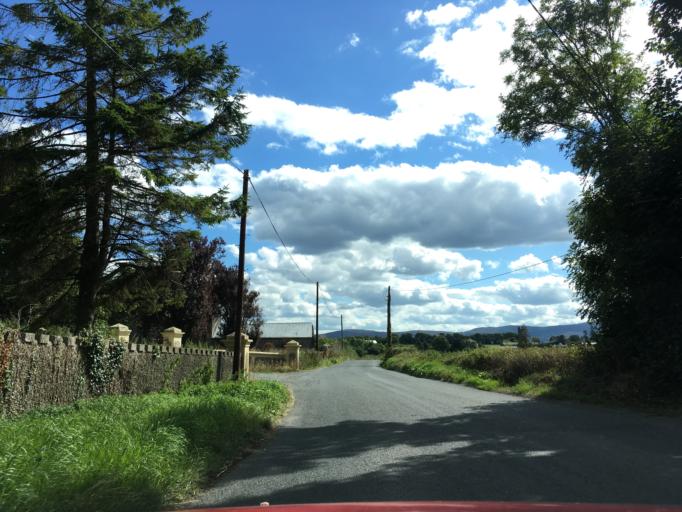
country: IE
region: Munster
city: Cashel
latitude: 52.4787
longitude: -7.9792
